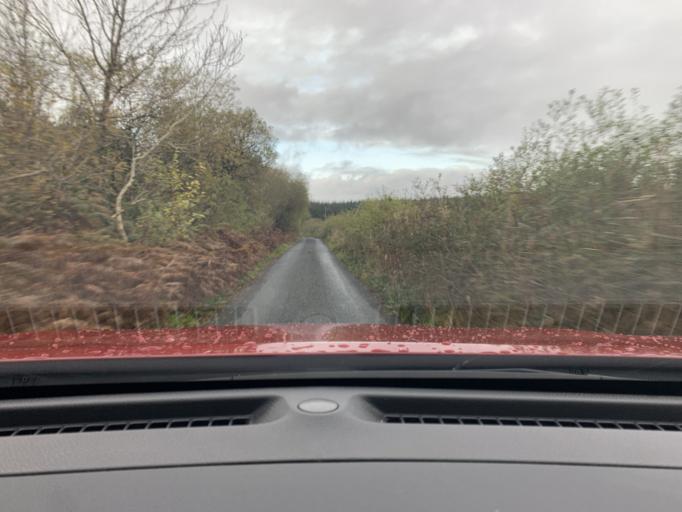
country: IE
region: Connaught
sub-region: Roscommon
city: Ballaghaderreen
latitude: 53.9701
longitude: -8.5954
